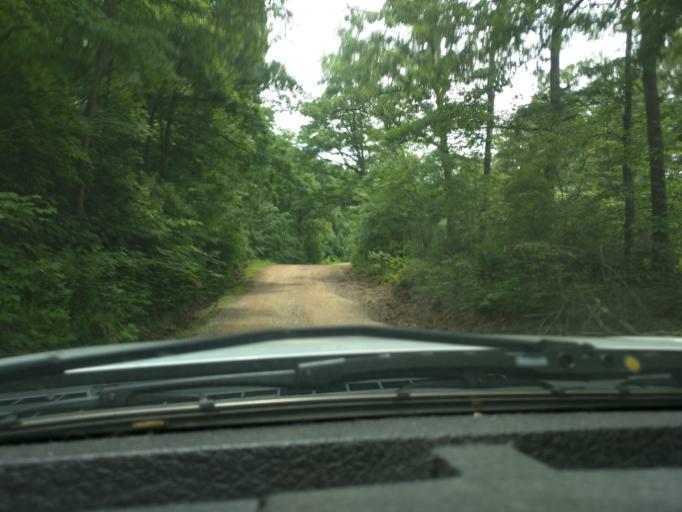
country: US
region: Arkansas
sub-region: Madison County
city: Huntsville
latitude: 35.8673
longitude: -93.5295
